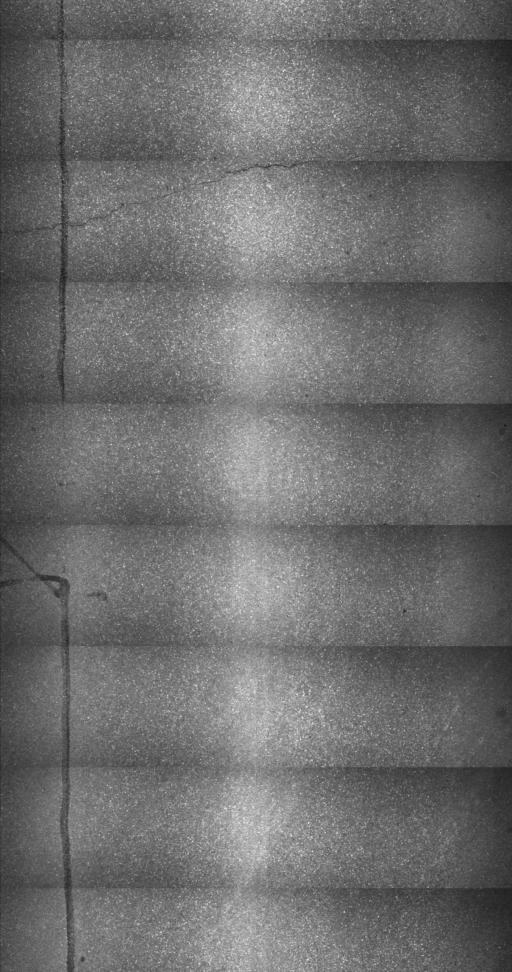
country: US
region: Vermont
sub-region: Franklin County
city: Saint Albans
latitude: 44.7328
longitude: -73.0472
